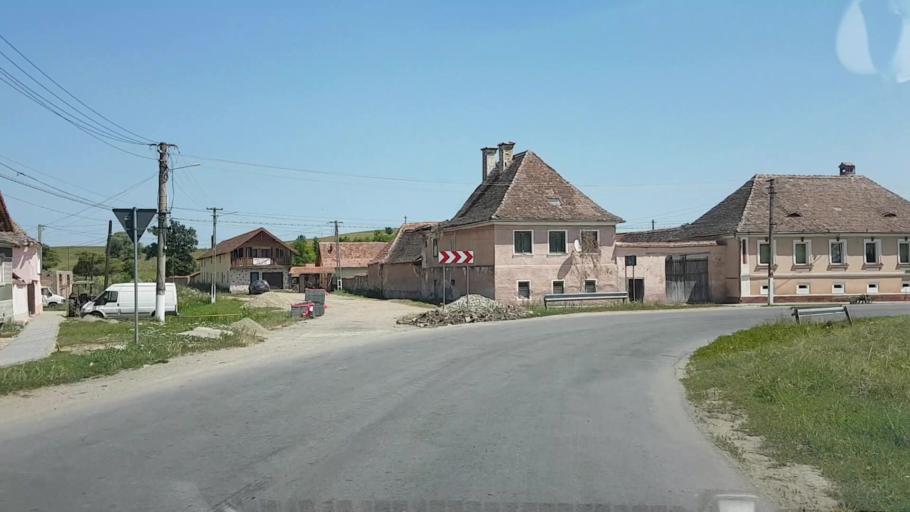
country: RO
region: Brasov
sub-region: Comuna Cincu
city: Cincu
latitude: 45.9181
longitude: 24.8048
